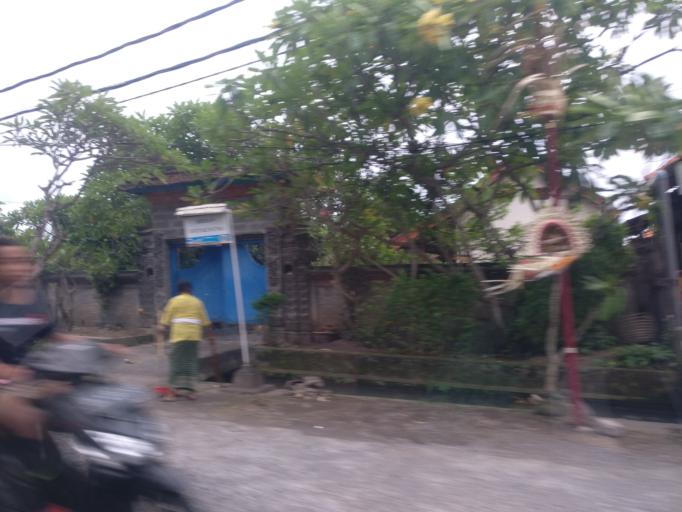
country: ID
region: Bali
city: Banjar Sedang
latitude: -8.5684
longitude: 115.2961
